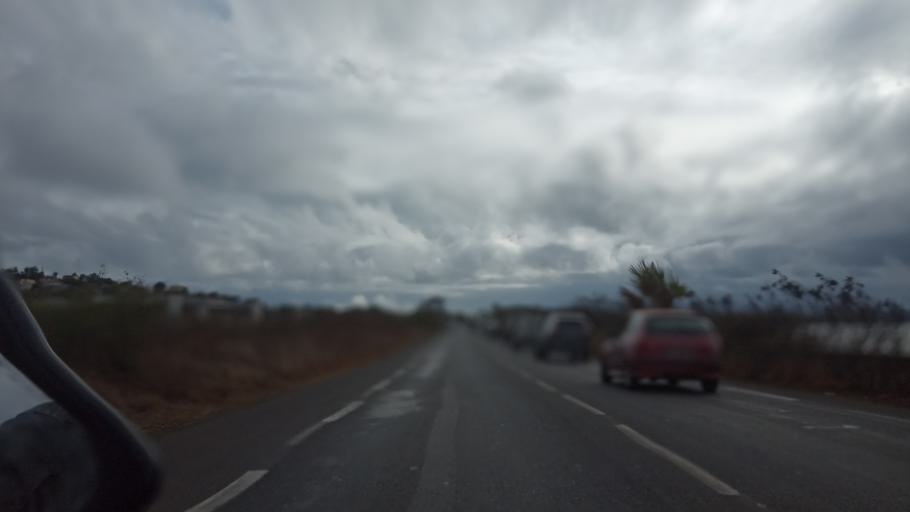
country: YT
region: Mamoudzou
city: Mamoudzou
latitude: -12.7923
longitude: 45.2208
